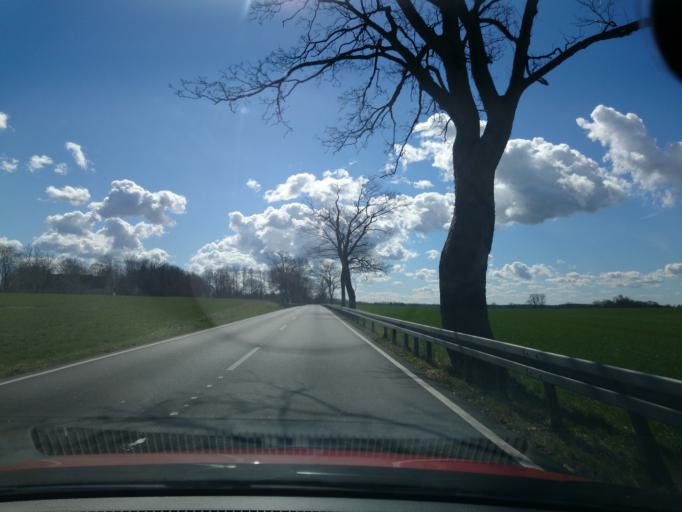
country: DE
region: Mecklenburg-Vorpommern
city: Barth
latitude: 54.3088
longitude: 12.7176
